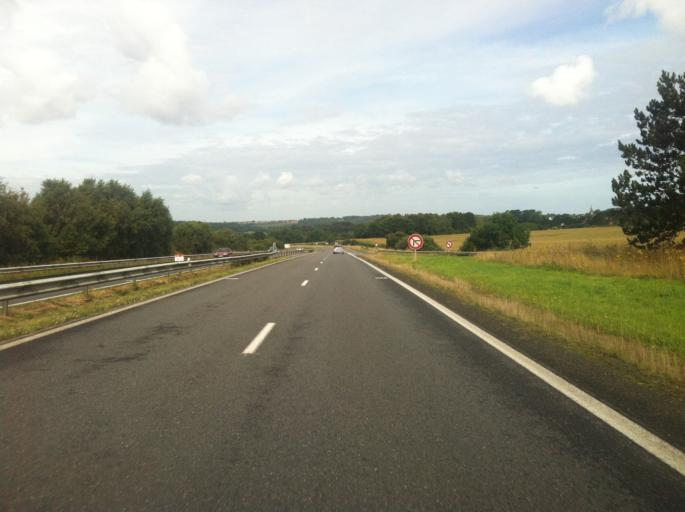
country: FR
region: Brittany
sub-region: Departement du Finistere
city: Morlaix
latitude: 48.5941
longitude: -3.8221
